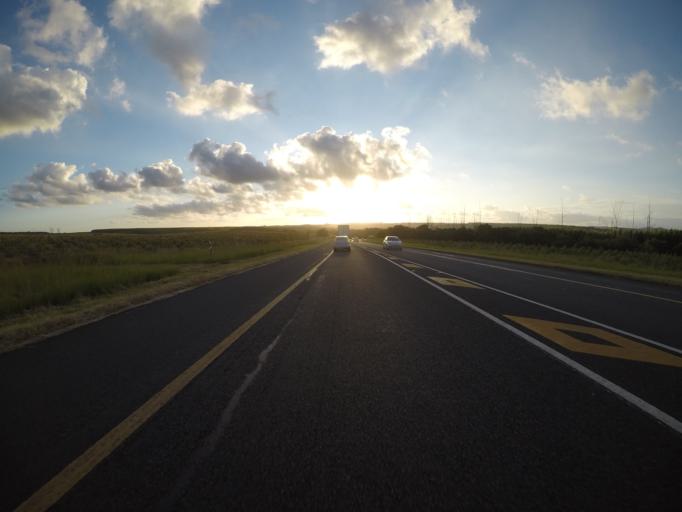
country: ZA
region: KwaZulu-Natal
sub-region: uThungulu District Municipality
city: Richards Bay
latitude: -28.6961
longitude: 32.0185
